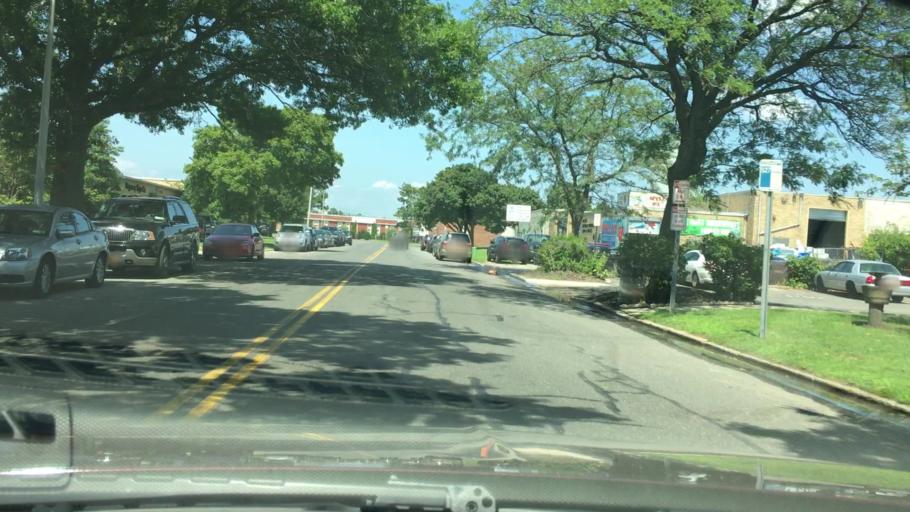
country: US
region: New York
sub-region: Suffolk County
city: Bay Wood
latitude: 40.7654
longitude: -73.2970
